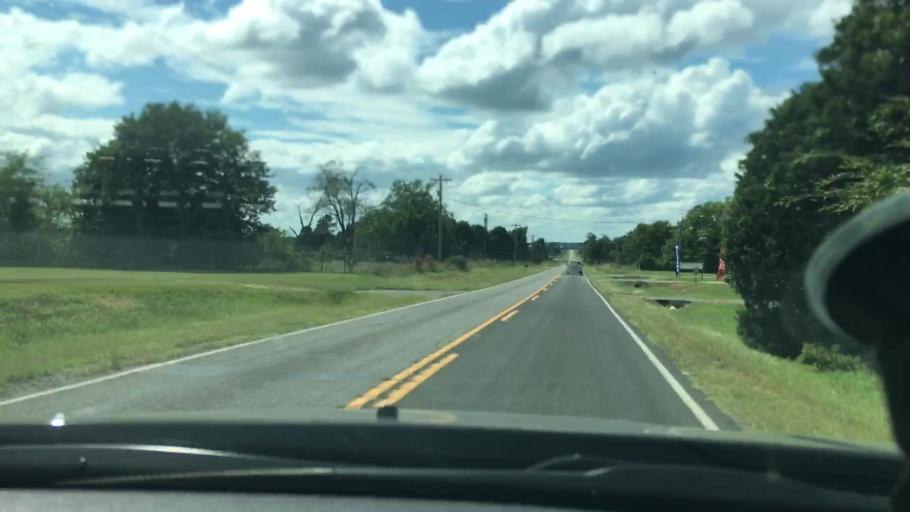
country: US
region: Oklahoma
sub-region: Sequoyah County
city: Vian
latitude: 35.6097
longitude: -94.9680
